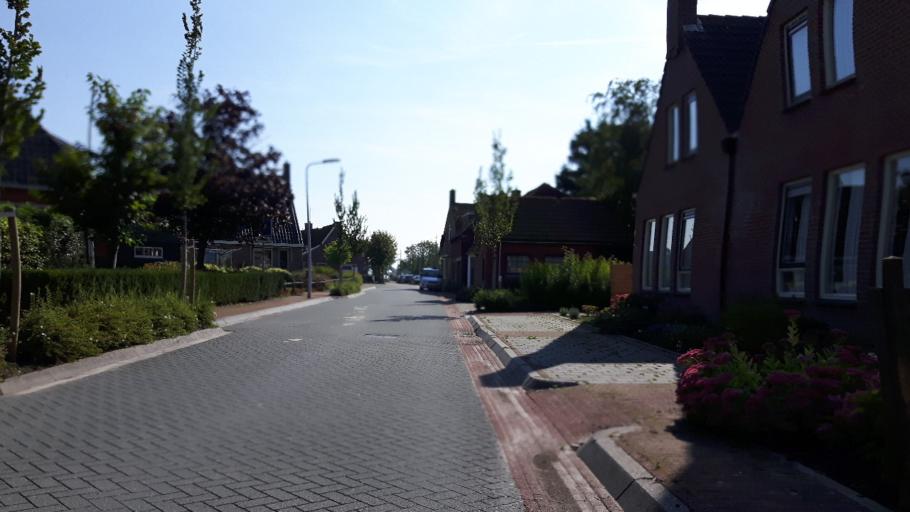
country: NL
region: Friesland
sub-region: Gemeente Ferwerderadiel
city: Ferwert
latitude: 53.3524
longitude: 5.8607
